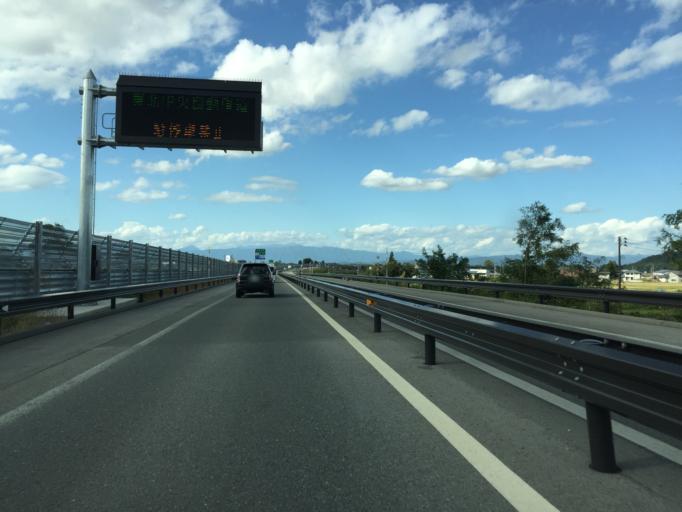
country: JP
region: Yamagata
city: Yonezawa
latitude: 37.9149
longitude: 140.1387
